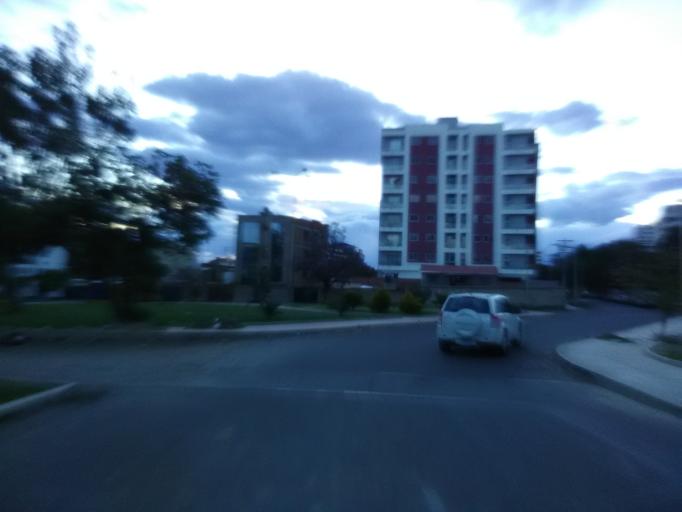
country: BO
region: Cochabamba
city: Cochabamba
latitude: -17.3751
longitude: -66.1453
